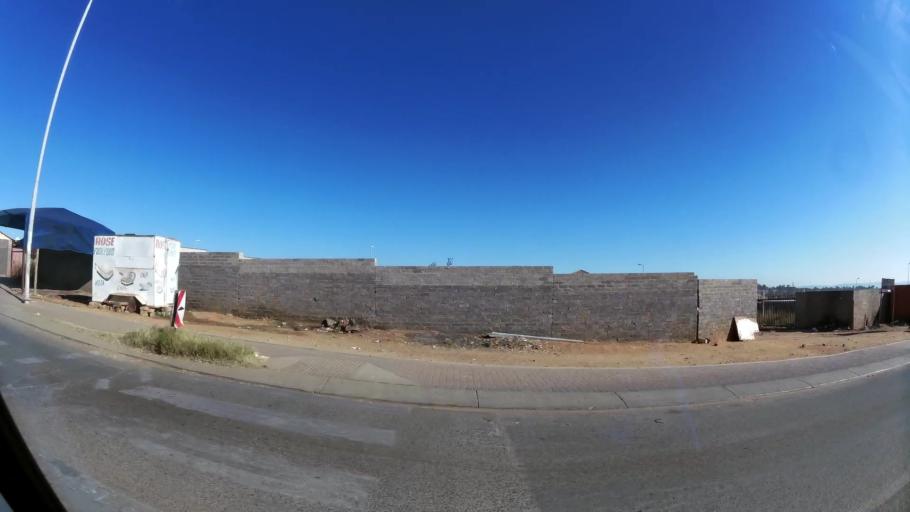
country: ZA
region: Gauteng
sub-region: City of Johannesburg Metropolitan Municipality
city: Diepsloot
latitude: -25.9003
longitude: 28.0981
